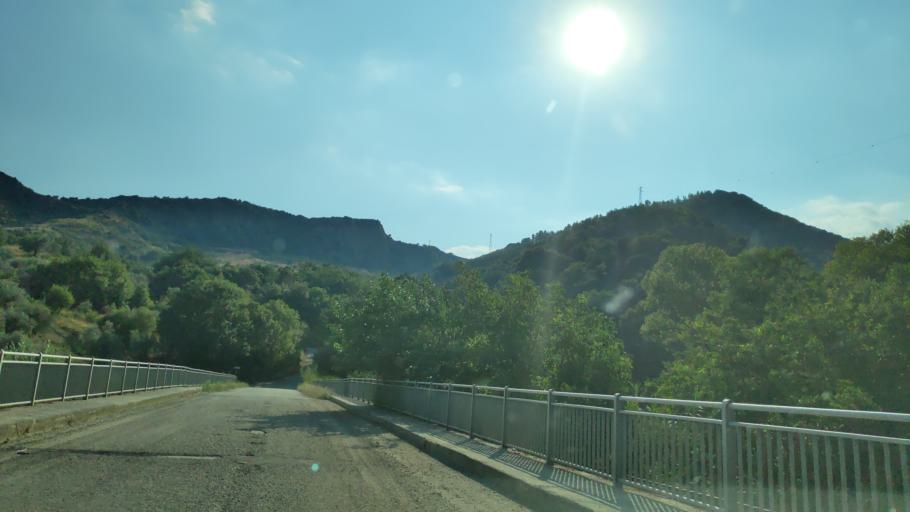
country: IT
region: Calabria
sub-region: Provincia di Reggio Calabria
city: Placanica
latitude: 38.4133
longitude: 16.4408
